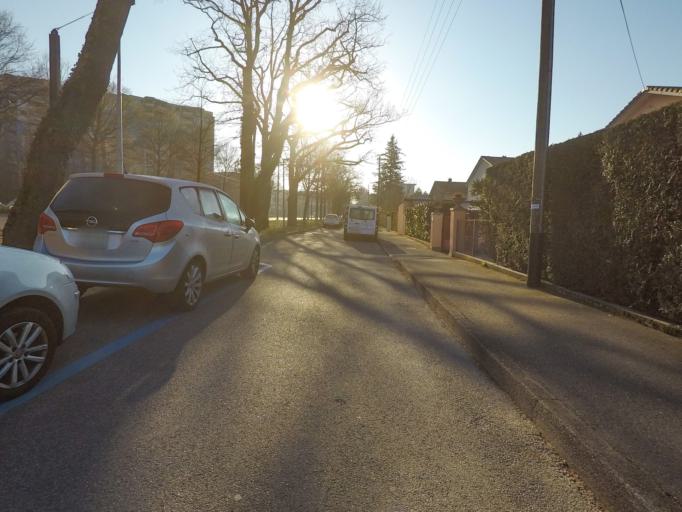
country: CH
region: Geneva
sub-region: Geneva
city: Les Avanchets
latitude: 46.2190
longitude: 6.1077
